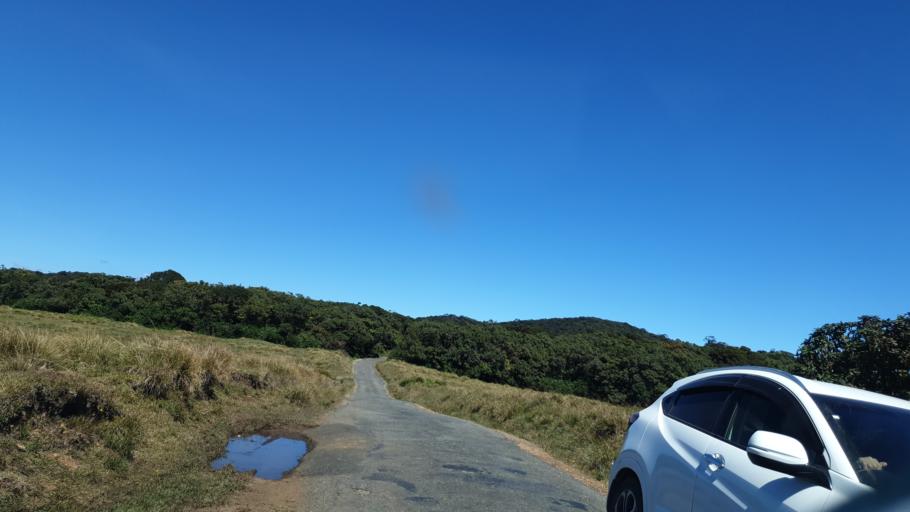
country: LK
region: Central
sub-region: Nuwara Eliya District
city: Nuwara Eliya
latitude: 6.8247
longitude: 80.8054
